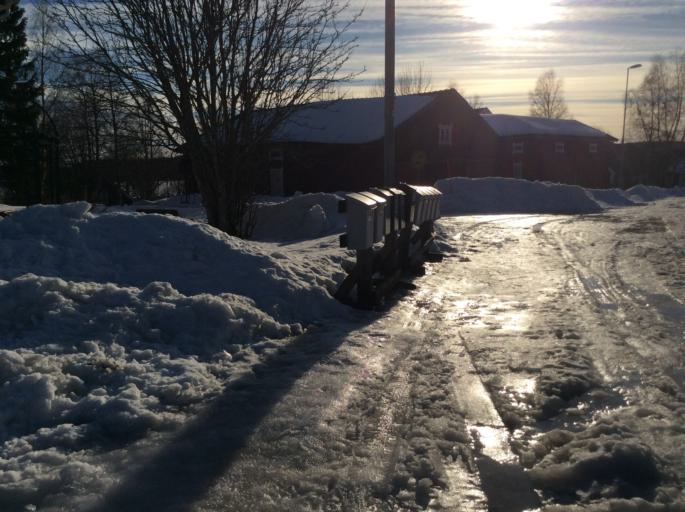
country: SE
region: Vaesterbotten
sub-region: Umea Kommun
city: Roback
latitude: 64.0387
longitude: 20.0741
